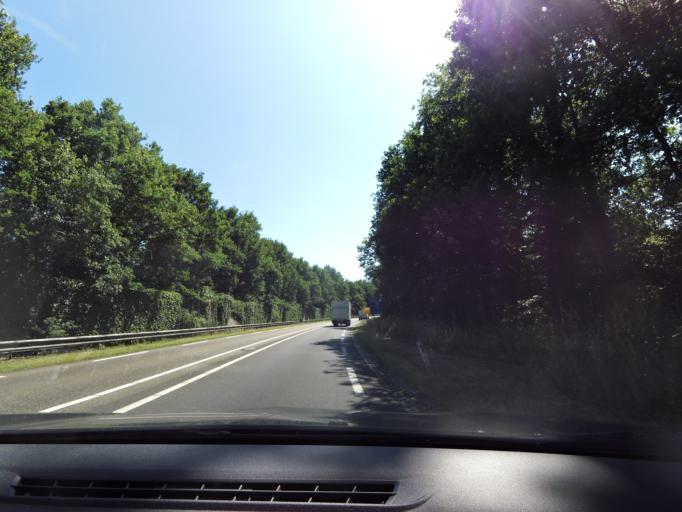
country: NL
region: Gelderland
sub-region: Berkelland
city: Eibergen
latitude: 52.0378
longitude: 6.6285
